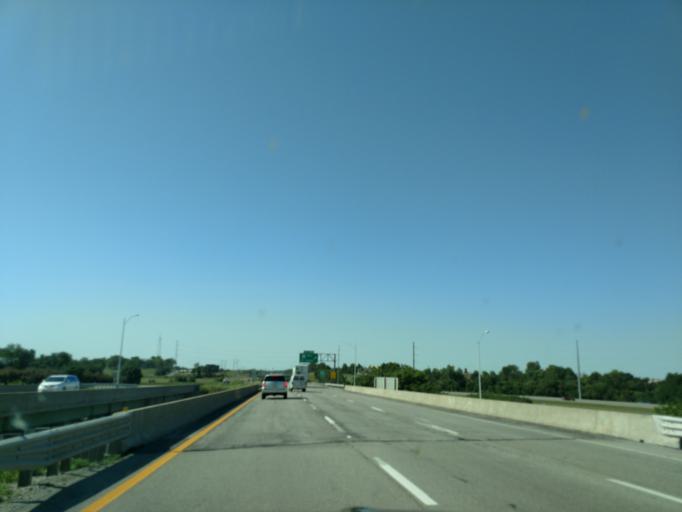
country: US
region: Missouri
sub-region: Buchanan County
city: Saint Joseph
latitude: 39.7486
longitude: -94.7894
